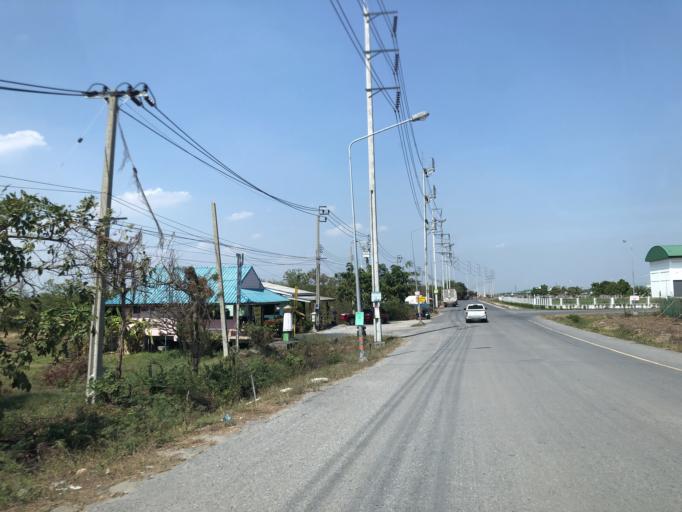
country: TH
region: Samut Prakan
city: Bang Bo District
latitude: 13.5053
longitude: 100.7437
